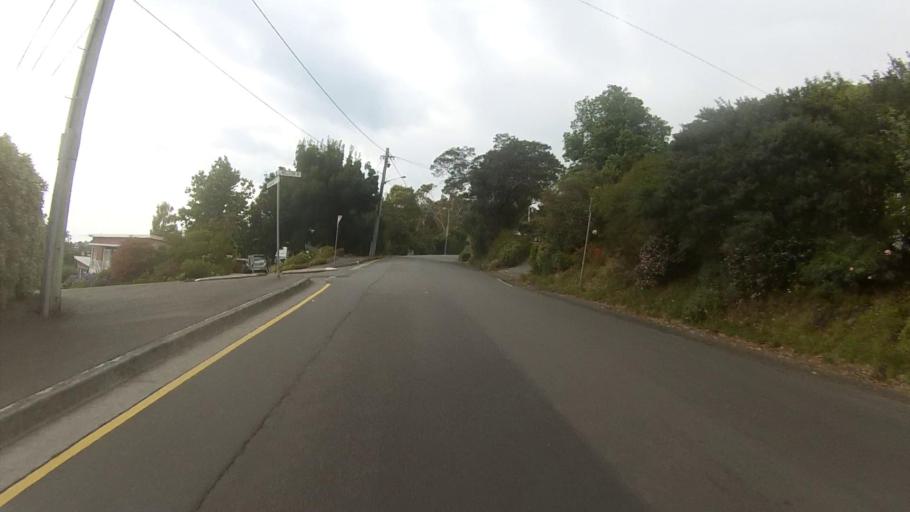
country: AU
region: Tasmania
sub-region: Hobart
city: Dynnyrne
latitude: -42.9081
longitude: 147.3281
